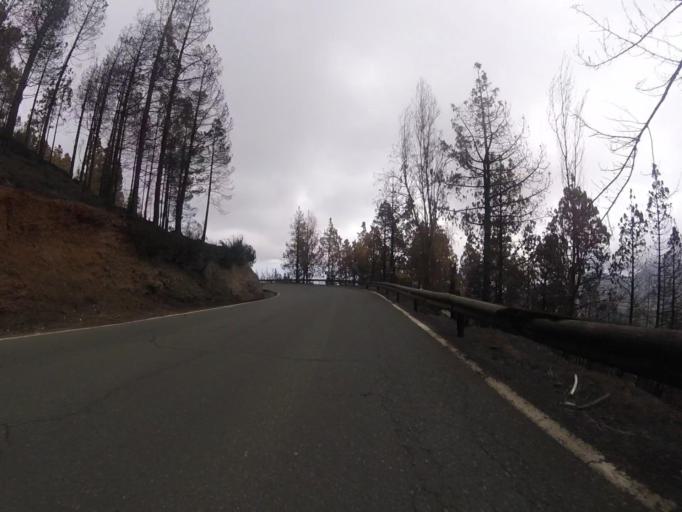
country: ES
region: Canary Islands
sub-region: Provincia de Las Palmas
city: Tejeda
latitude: 27.9834
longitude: -15.5790
